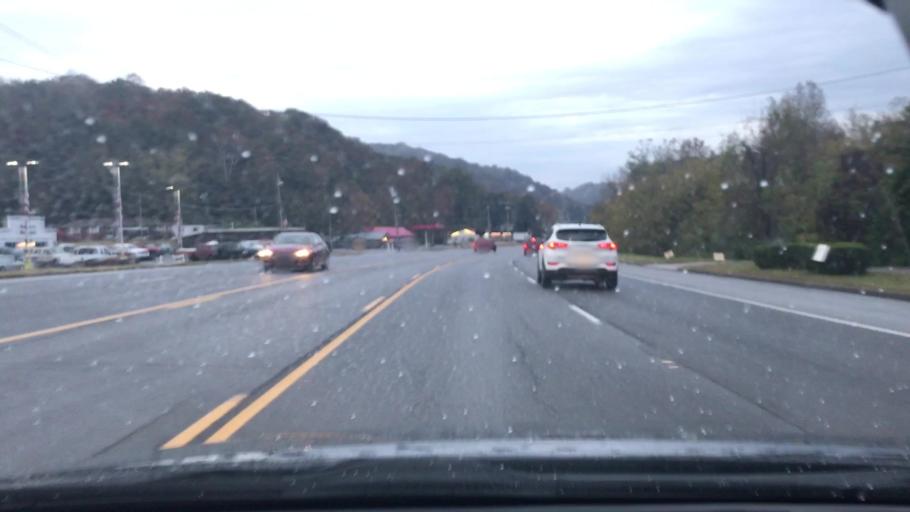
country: US
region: Tennessee
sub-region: Cheatham County
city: Ashland City
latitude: 36.2600
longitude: -87.0458
